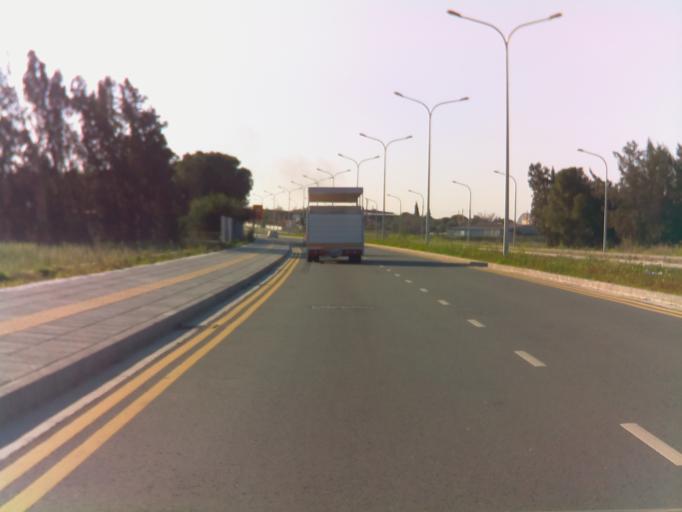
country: CY
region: Limassol
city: Ypsonas
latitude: 34.6738
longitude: 32.9889
